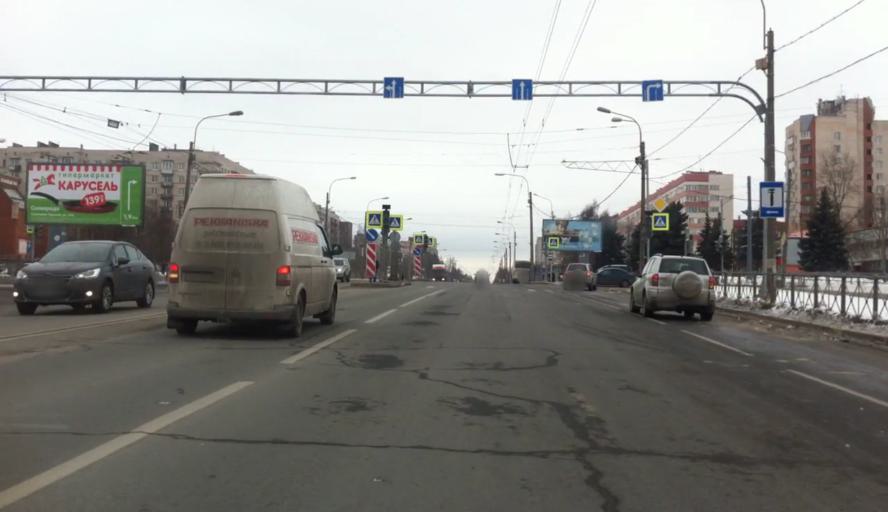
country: RU
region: St.-Petersburg
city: Uritsk
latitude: 59.8430
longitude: 30.1753
